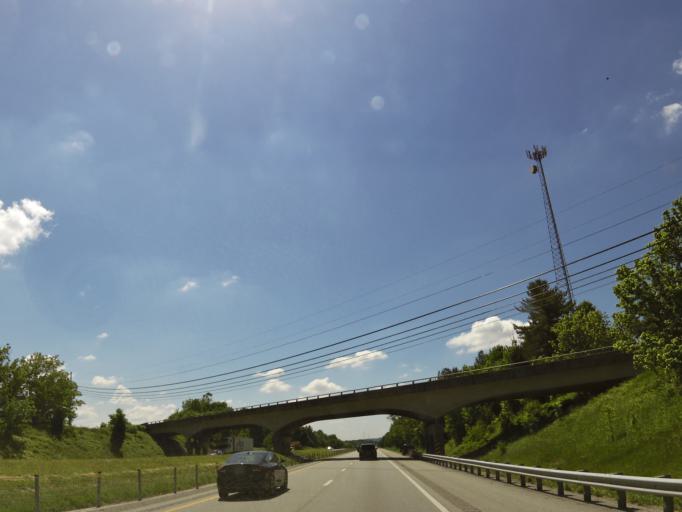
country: US
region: Kentucky
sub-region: Laurel County
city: London
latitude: 37.1897
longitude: -84.1446
